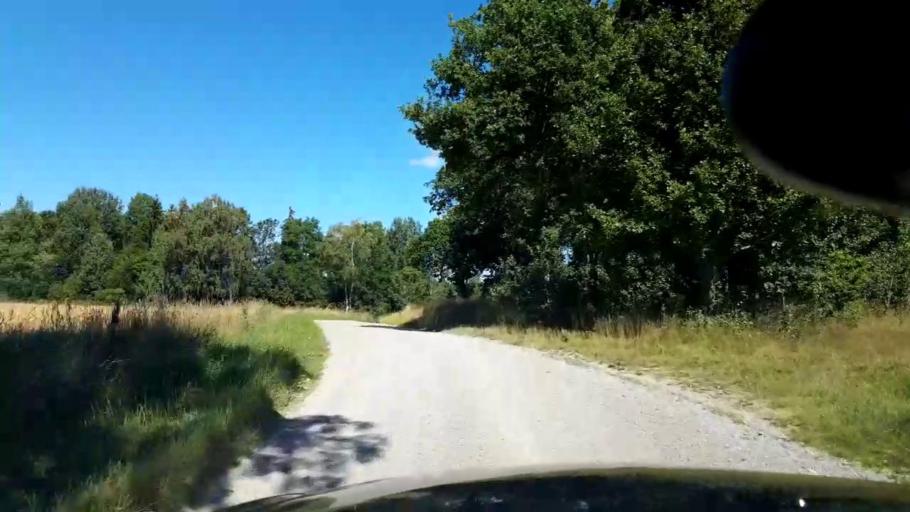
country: SE
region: Stockholm
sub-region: Sigtuna Kommun
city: Sigtuna
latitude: 59.6136
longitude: 17.6376
